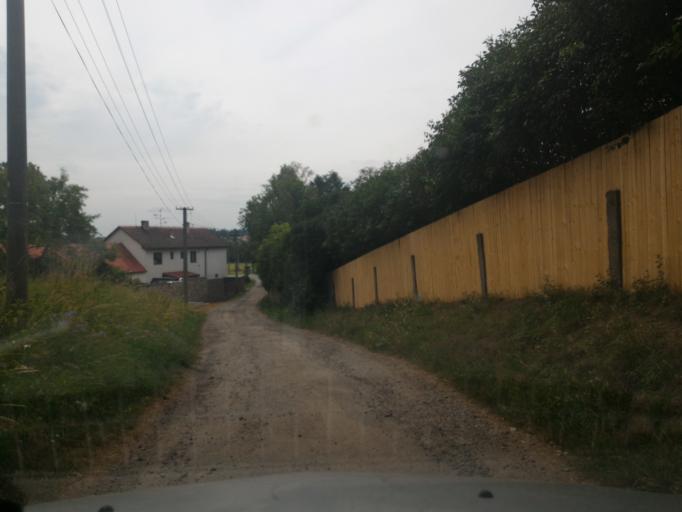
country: CZ
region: Vysocina
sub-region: Okres Jihlava
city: Telc
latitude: 49.1935
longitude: 15.4497
